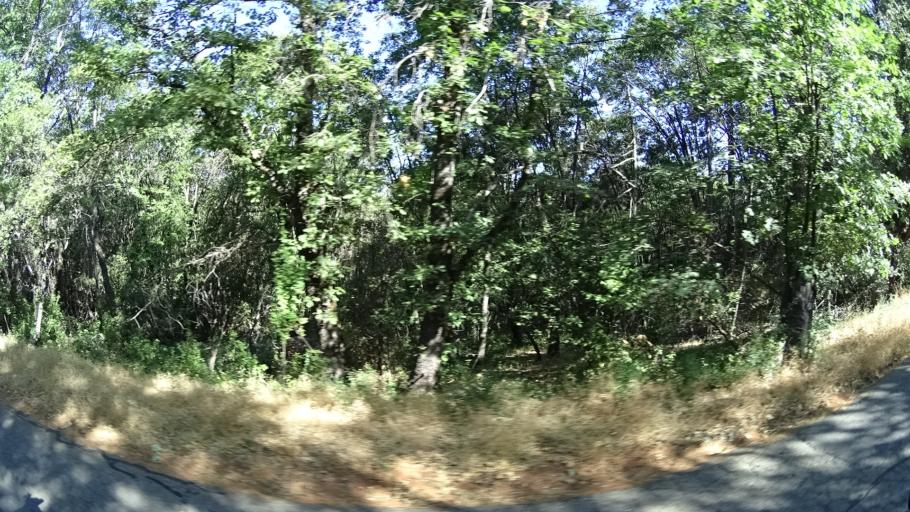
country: US
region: California
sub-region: Amador County
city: Pioneer
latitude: 38.3990
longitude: -120.5429
